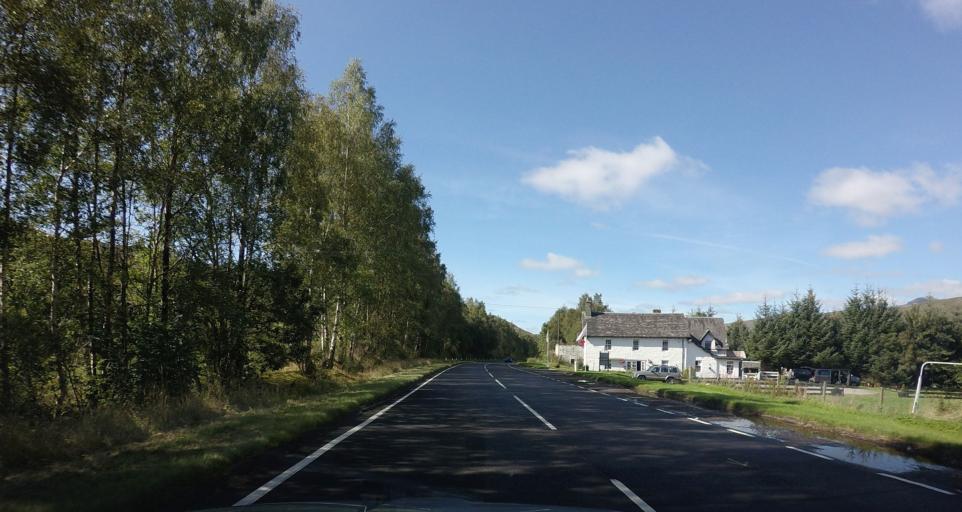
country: GB
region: Scotland
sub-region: Stirling
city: Callander
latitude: 56.4191
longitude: -4.4418
